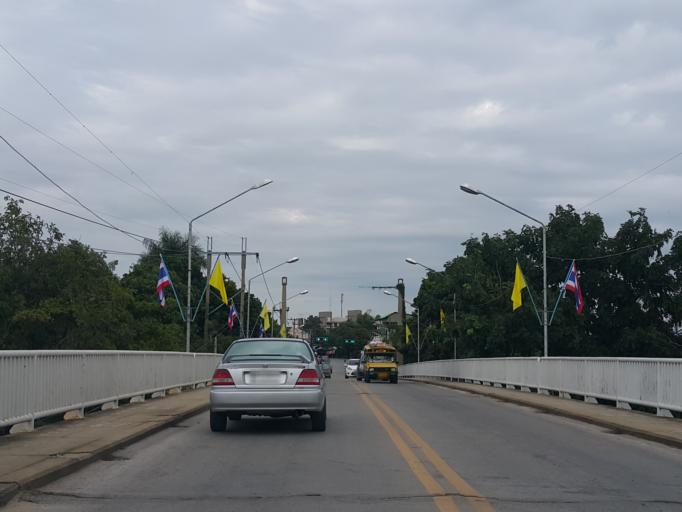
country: TH
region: Lampang
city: Lampang
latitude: 18.2942
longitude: 99.4898
